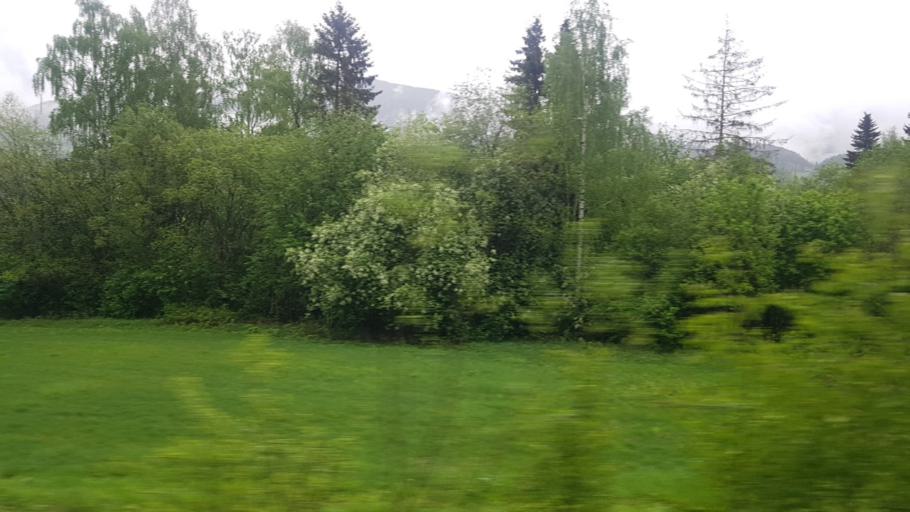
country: NO
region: Oppland
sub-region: Ringebu
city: Ringebu
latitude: 61.4470
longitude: 10.2023
